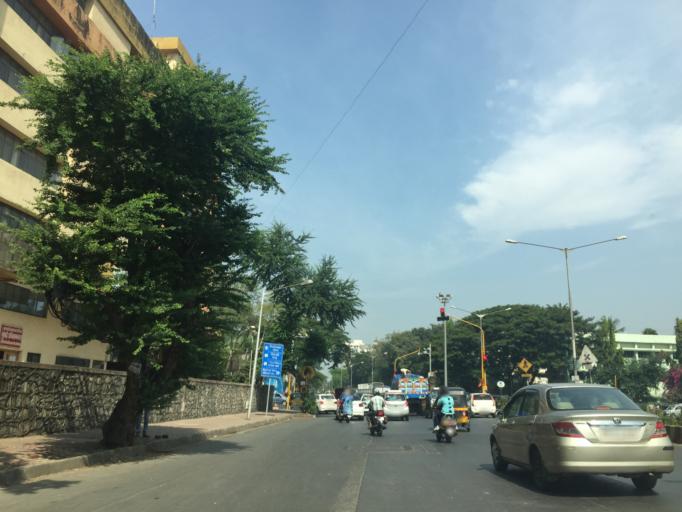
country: IN
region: Maharashtra
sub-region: Mumbai Suburban
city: Borivli
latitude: 19.2294
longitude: 72.8409
